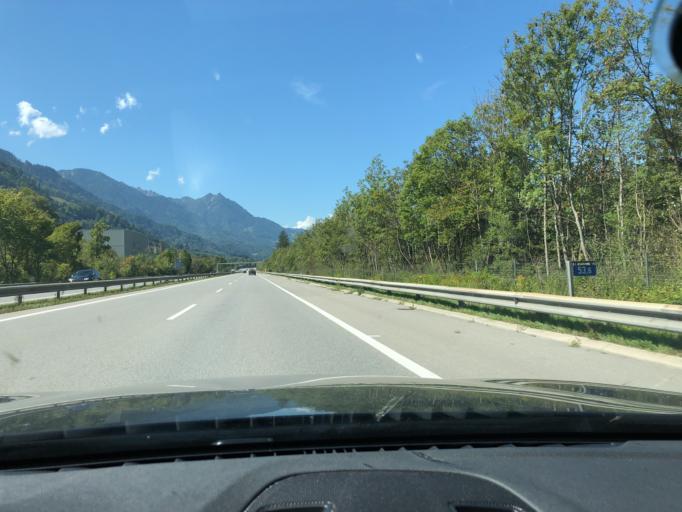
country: AT
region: Vorarlberg
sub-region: Politischer Bezirk Bludenz
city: Thuringen
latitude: 47.1752
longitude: 9.7550
